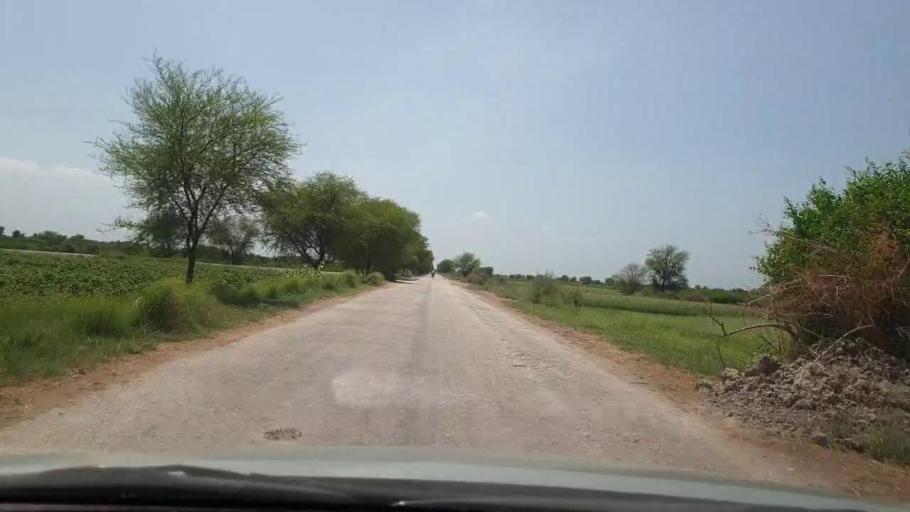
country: PK
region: Sindh
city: Pano Aqil
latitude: 27.6636
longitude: 69.1231
